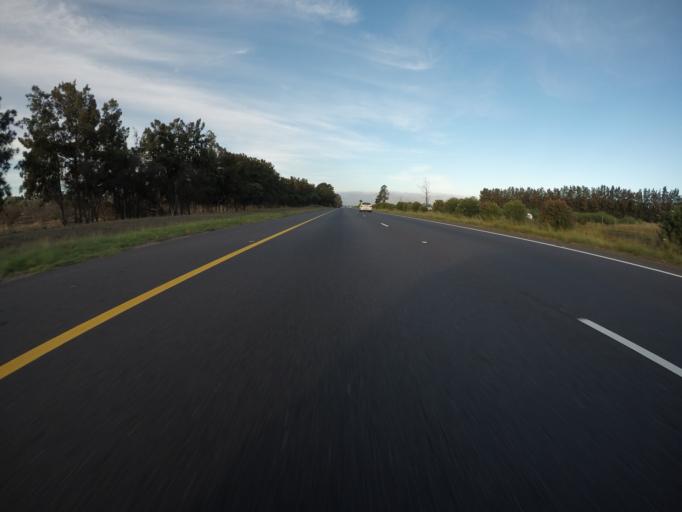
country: ZA
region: Western Cape
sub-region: City of Cape Town
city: Kraaifontein
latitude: -33.8077
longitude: 18.8347
